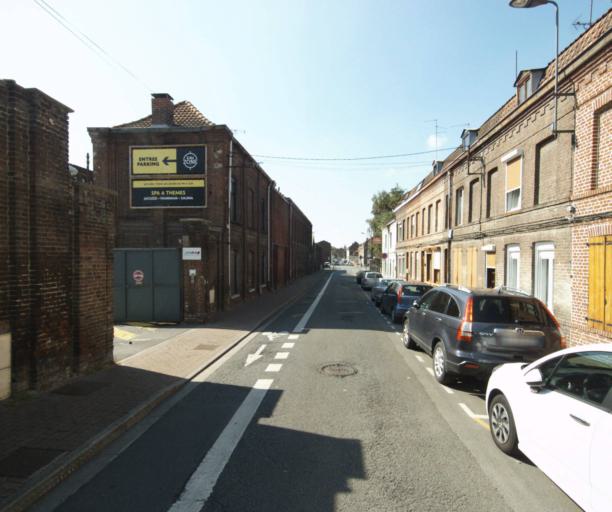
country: FR
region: Nord-Pas-de-Calais
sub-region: Departement du Nord
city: Mons-en-Baroeul
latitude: 50.6348
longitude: 3.1148
